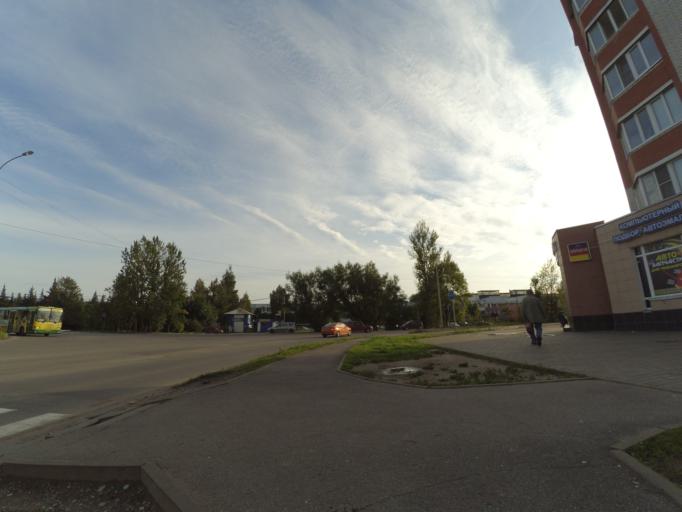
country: RU
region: Novgorod
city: Pankovka
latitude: 58.5254
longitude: 31.2184
